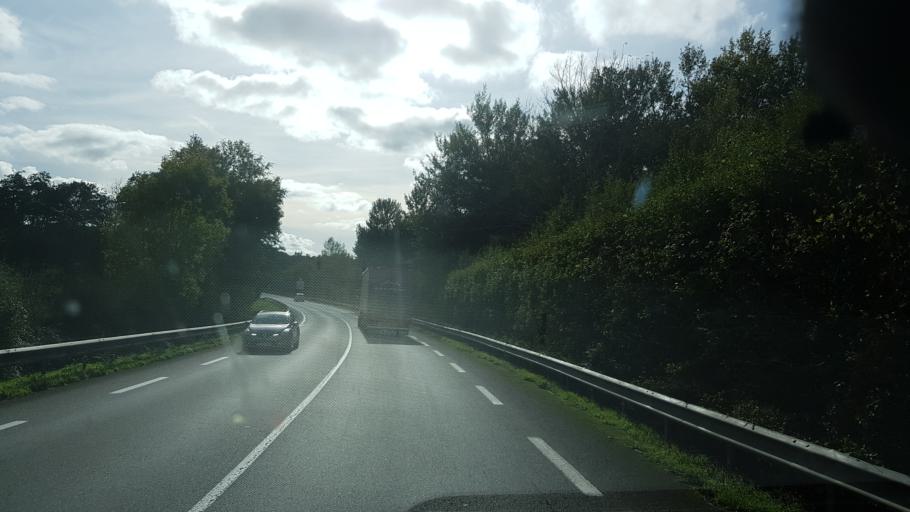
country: FR
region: Poitou-Charentes
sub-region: Departement de la Charente
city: Confolens
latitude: 46.0414
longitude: 0.6596
